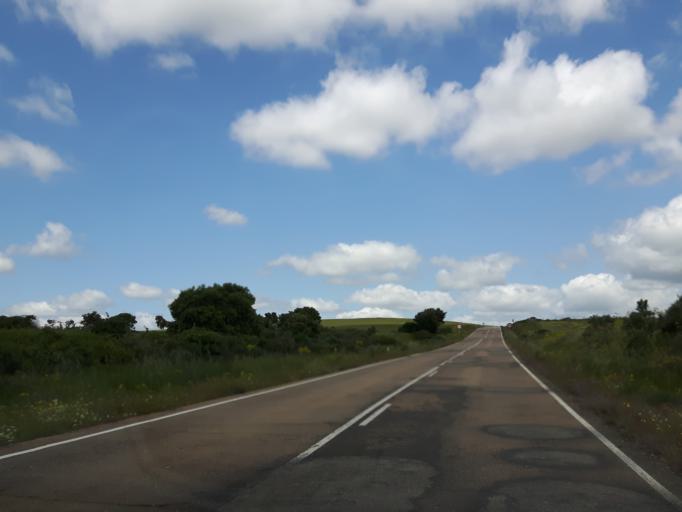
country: ES
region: Castille and Leon
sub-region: Provincia de Salamanca
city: Villar de la Yegua
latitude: 40.7162
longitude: -6.6928
